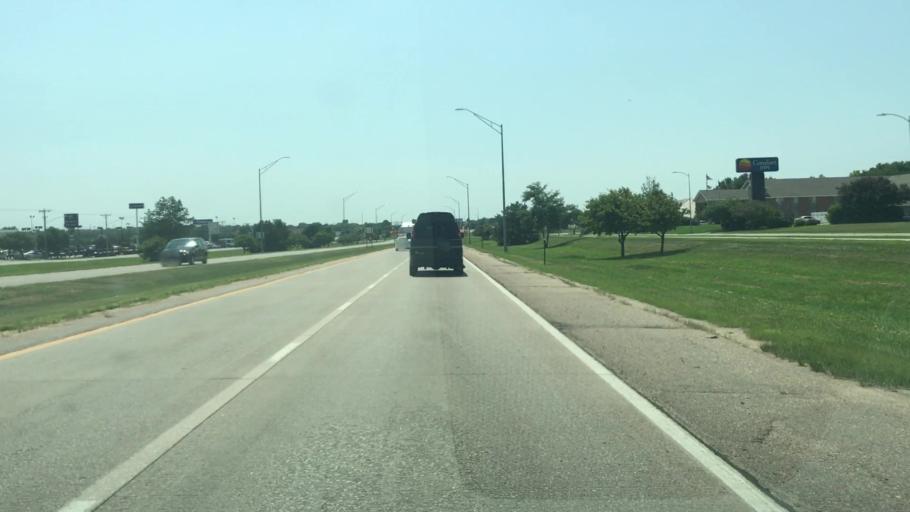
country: US
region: Nebraska
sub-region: Adams County
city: Hastings
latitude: 40.6171
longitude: -98.3832
